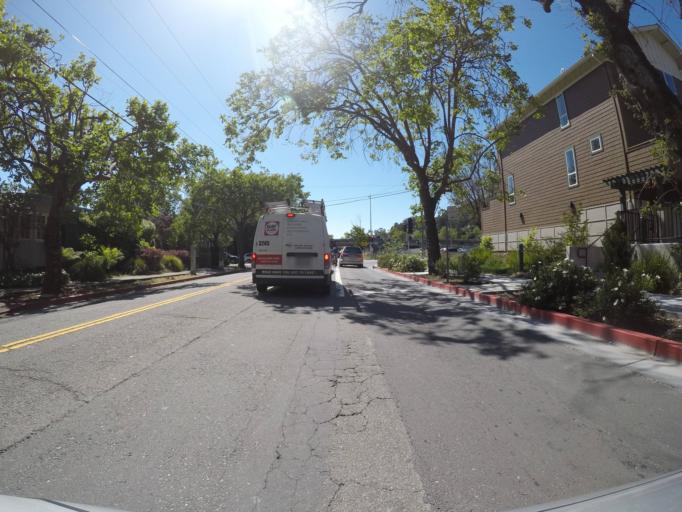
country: US
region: California
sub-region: Marin County
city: San Rafael
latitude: 37.9738
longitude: -122.5198
